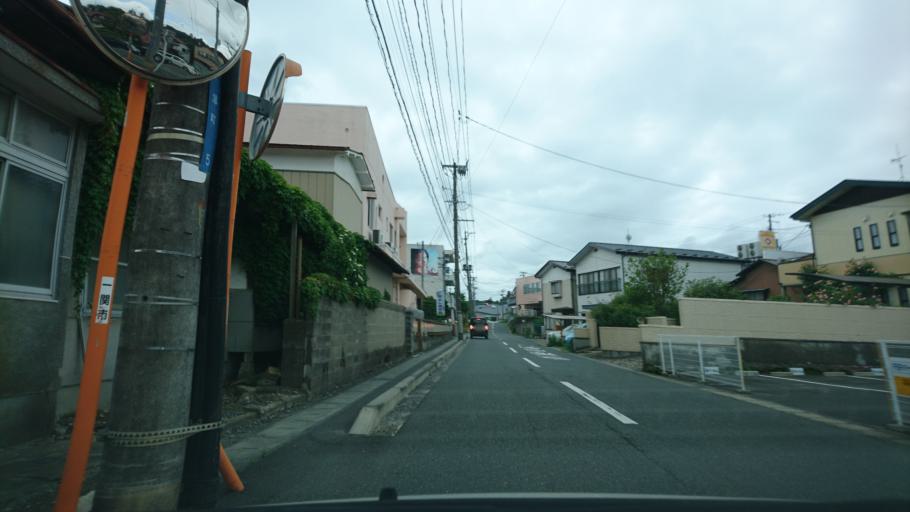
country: JP
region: Iwate
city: Ichinoseki
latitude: 38.9186
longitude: 141.1324
